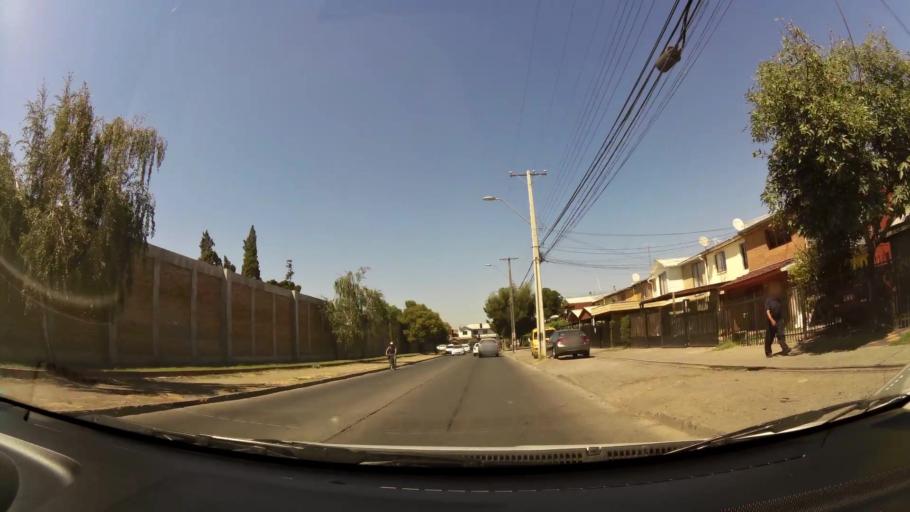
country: CL
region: Maule
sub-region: Provincia de Curico
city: Curico
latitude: -34.9761
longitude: -71.2354
